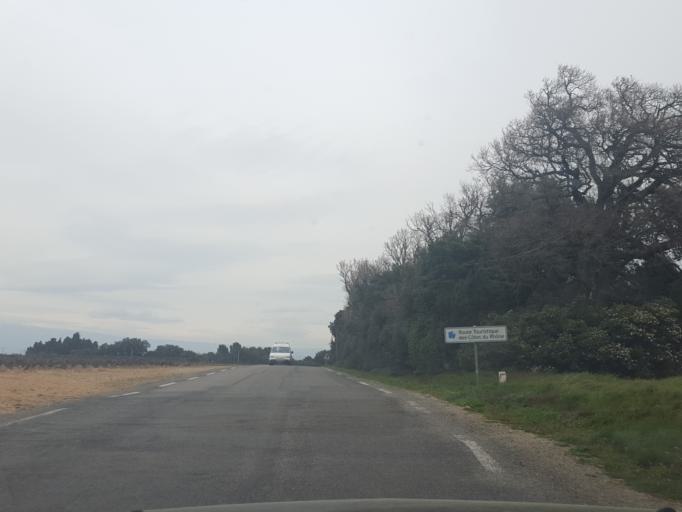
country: FR
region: Provence-Alpes-Cote d'Azur
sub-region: Departement du Vaucluse
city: Saint-Saturnin-les-Avignon
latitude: 43.9462
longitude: 4.9219
